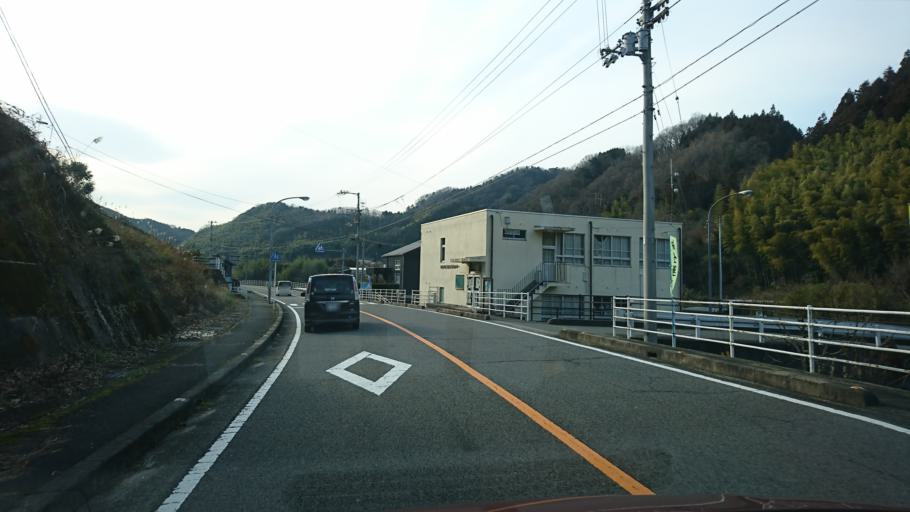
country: JP
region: Ehime
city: Hojo
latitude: 33.9001
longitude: 132.8687
